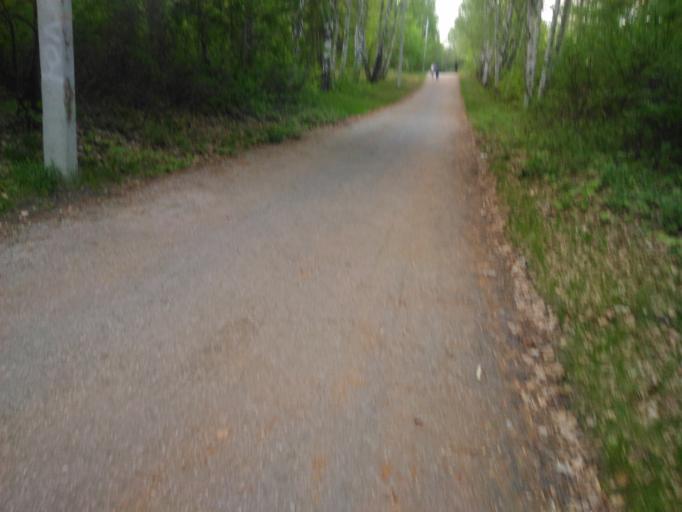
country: RU
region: Ulyanovsk
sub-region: Ulyanovskiy Rayon
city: Ulyanovsk
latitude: 54.2724
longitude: 48.3548
